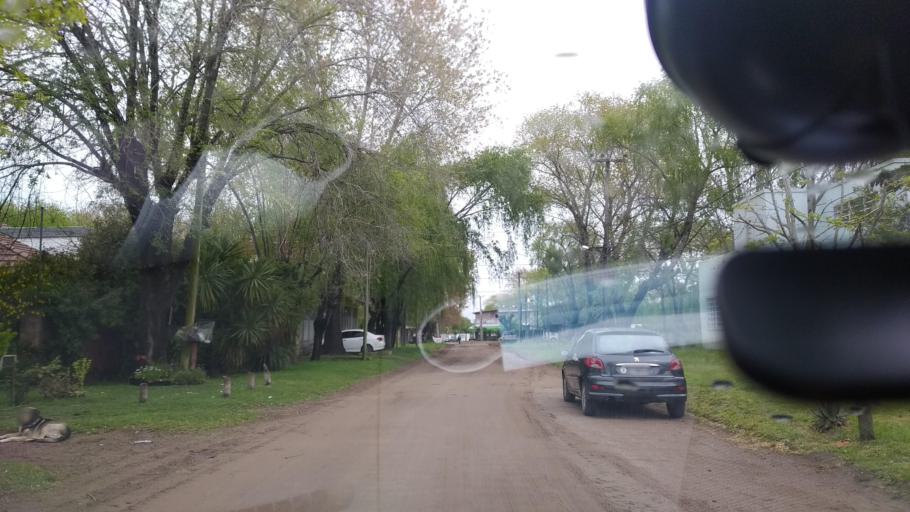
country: AR
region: Buenos Aires
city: Mar del Tuyu
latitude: -36.5324
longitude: -56.7119
